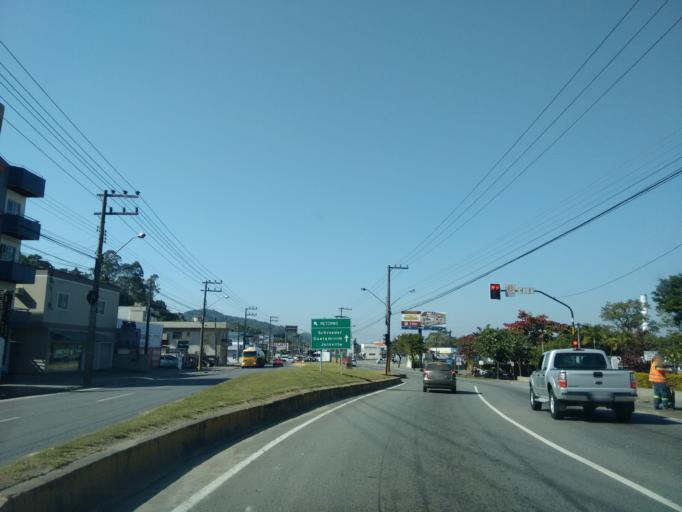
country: BR
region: Santa Catarina
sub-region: Jaragua Do Sul
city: Jaragua do Sul
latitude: -26.4781
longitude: -49.0496
